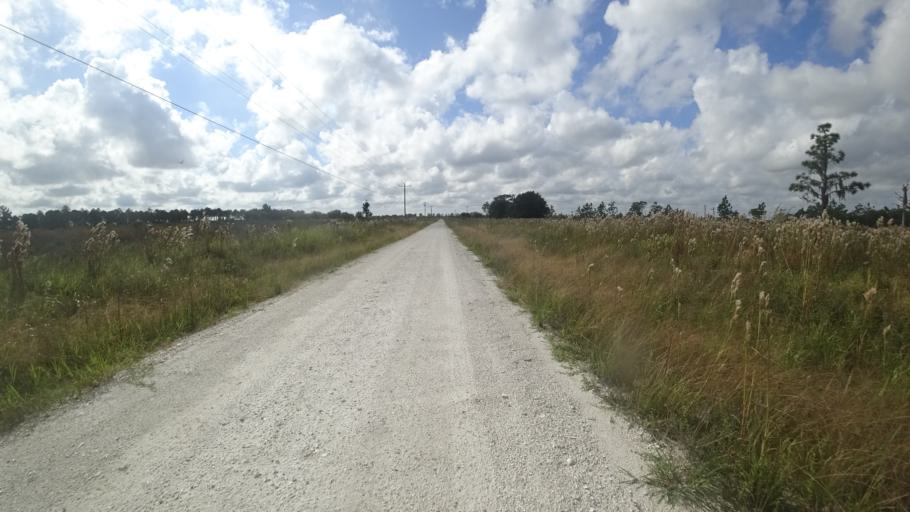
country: US
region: Florida
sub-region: Hillsborough County
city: Wimauma
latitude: 27.5394
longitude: -82.1286
